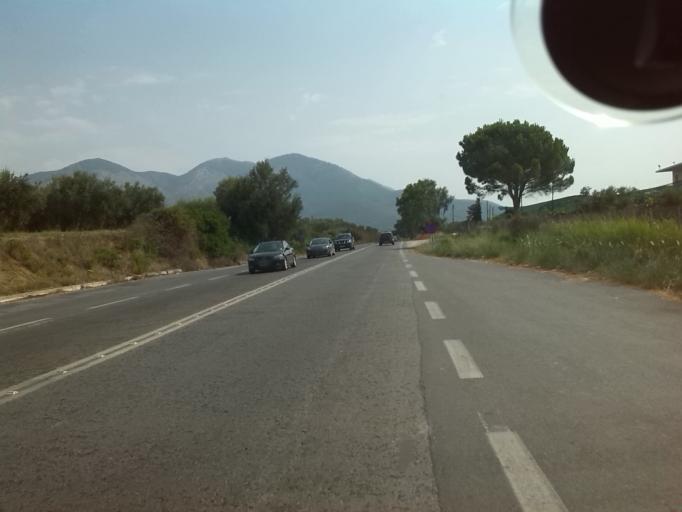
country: GR
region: Peloponnese
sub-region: Nomos Messinias
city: Kyparissia
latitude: 37.2853
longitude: 21.7020
